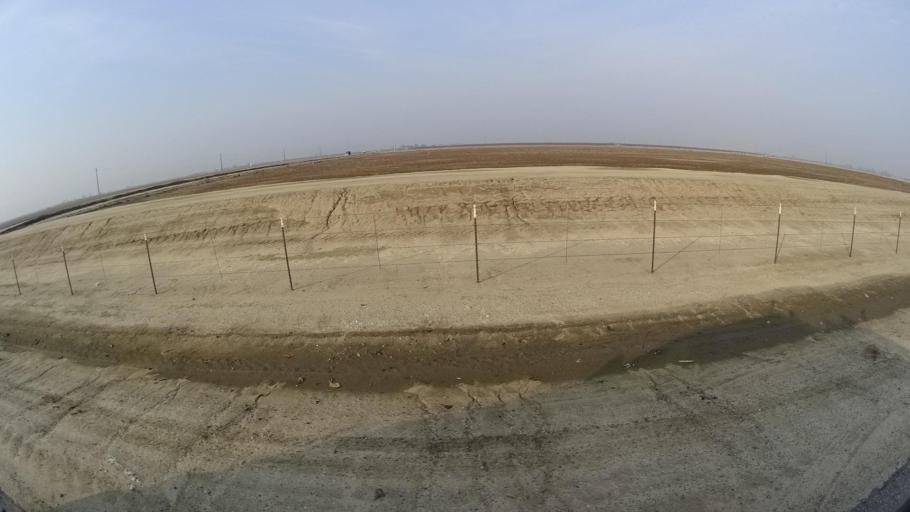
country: US
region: California
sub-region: Kern County
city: Greenfield
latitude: 35.2386
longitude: -119.0214
